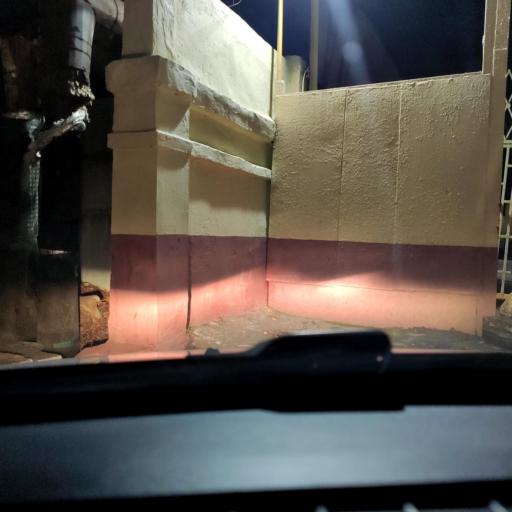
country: RU
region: Voronezj
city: Voronezh
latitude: 51.6546
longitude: 39.1616
